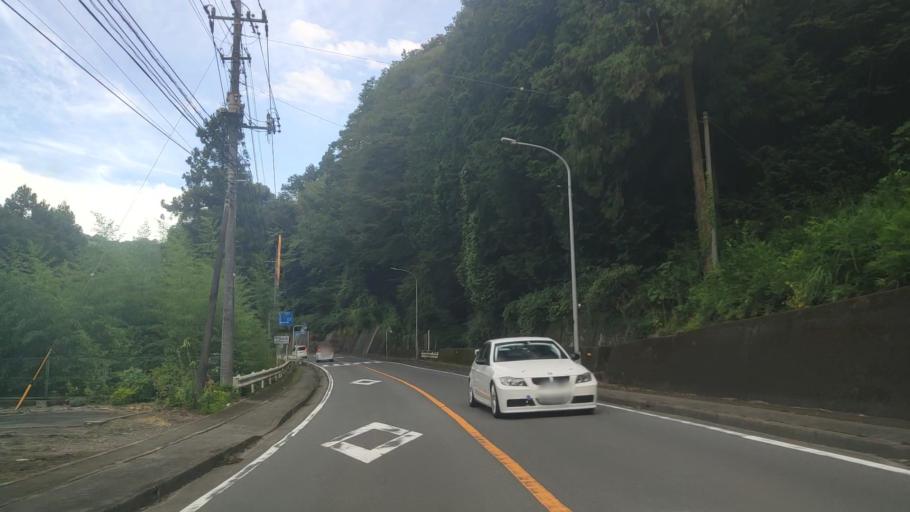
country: JP
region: Gunma
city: Omamacho-omama
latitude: 36.4977
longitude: 139.2747
